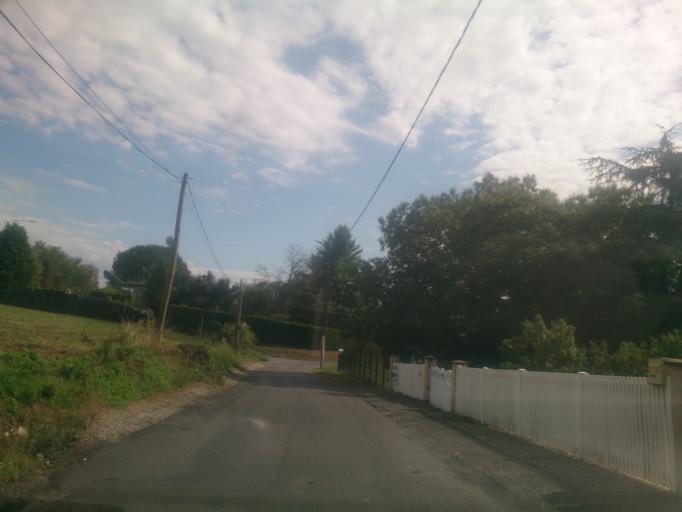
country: FR
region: Limousin
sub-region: Departement de la Correze
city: Malemort-sur-Correze
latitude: 45.1798
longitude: 1.5437
